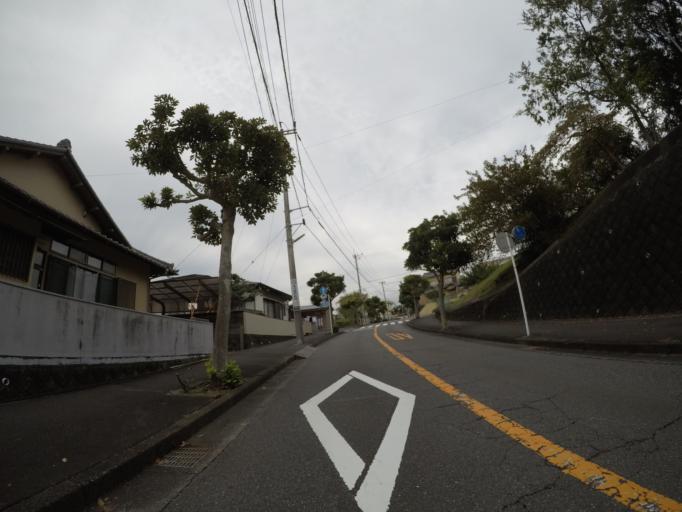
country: JP
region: Shizuoka
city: Fuji
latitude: 35.1835
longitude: 138.7080
